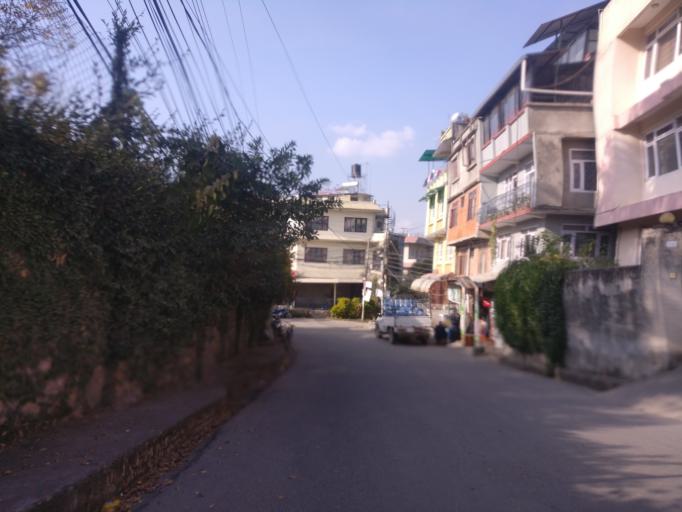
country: NP
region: Central Region
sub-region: Bagmati Zone
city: Patan
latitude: 27.6841
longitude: 85.3231
